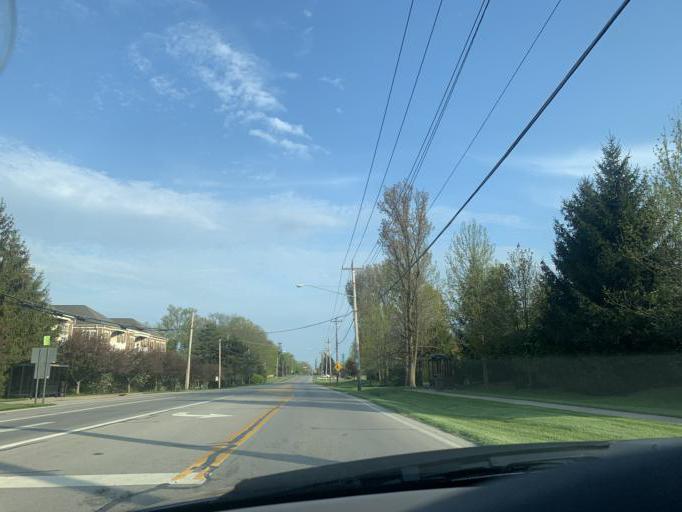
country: US
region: Ohio
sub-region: Hamilton County
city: Springdale
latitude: 39.2783
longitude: -84.4824
